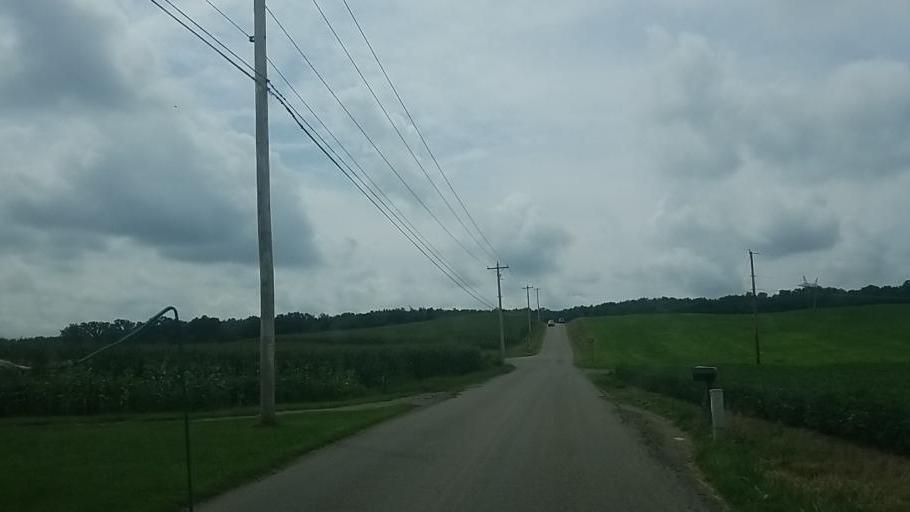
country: US
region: Ohio
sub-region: Knox County
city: Gambier
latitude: 40.4010
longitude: -82.3695
